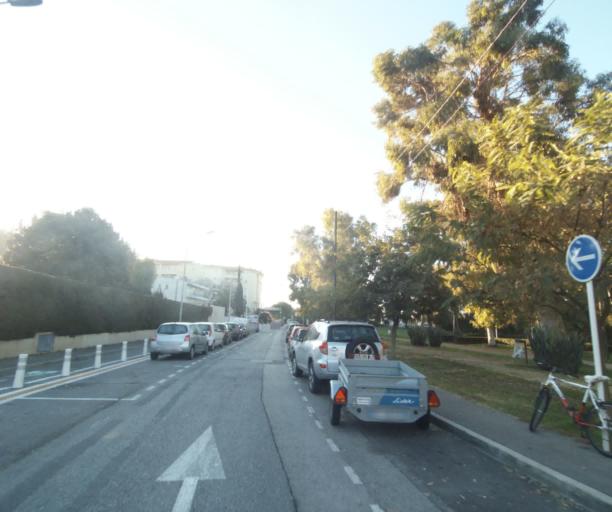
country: FR
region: Provence-Alpes-Cote d'Azur
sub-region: Departement des Alpes-Maritimes
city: Vallauris
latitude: 43.5744
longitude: 7.0870
